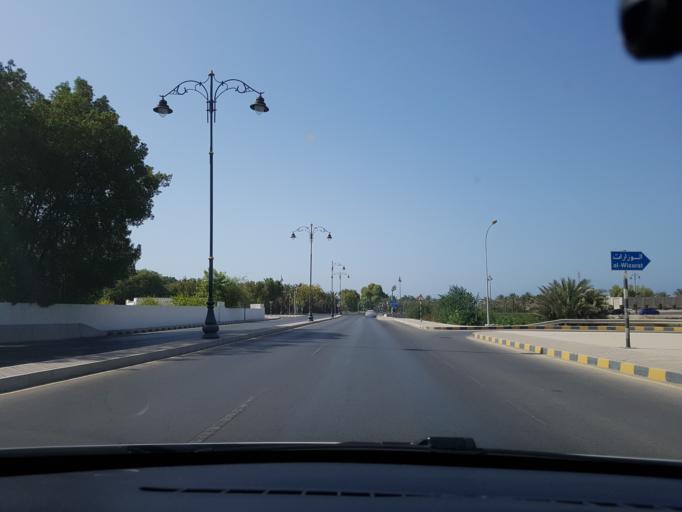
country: OM
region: Muhafazat Masqat
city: Bawshar
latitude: 23.5993
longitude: 58.4390
